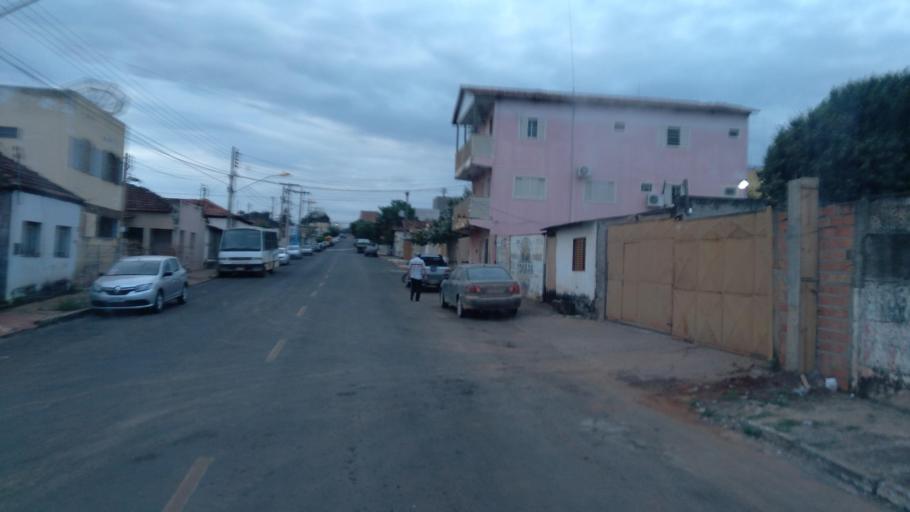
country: BR
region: Goias
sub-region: Mineiros
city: Mineiros
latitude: -17.5673
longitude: -52.5500
